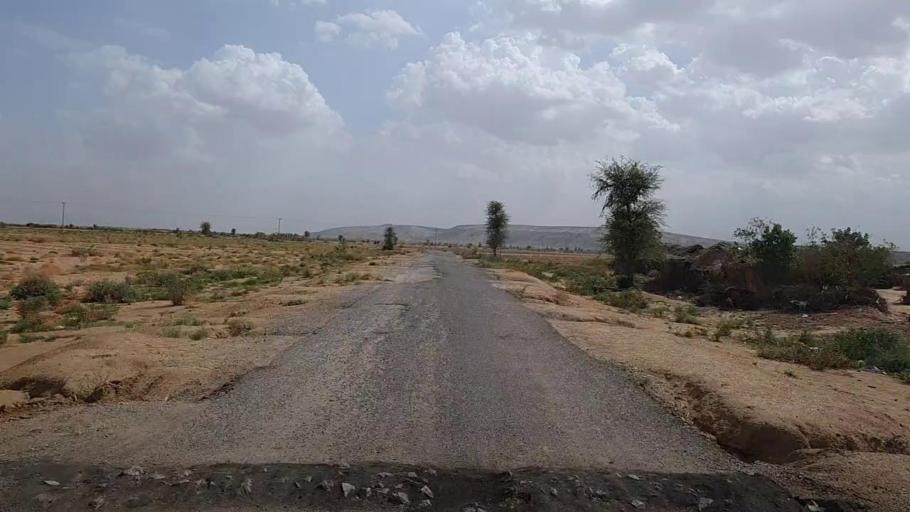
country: PK
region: Sindh
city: Jamshoro
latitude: 25.4015
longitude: 67.7673
